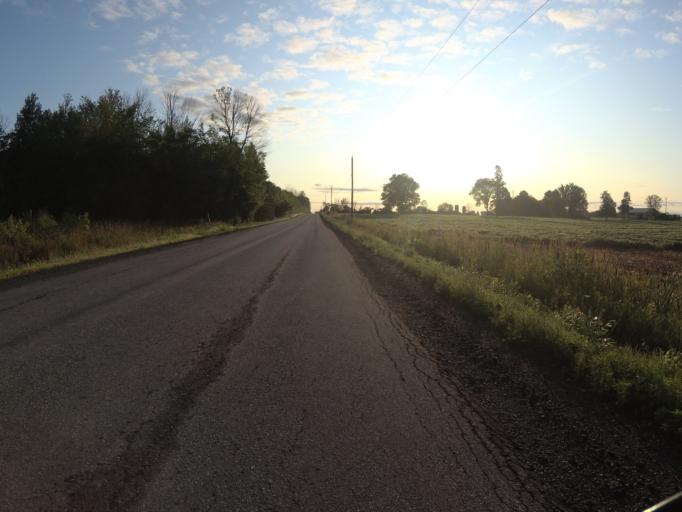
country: CA
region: Ontario
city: Casselman
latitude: 45.1540
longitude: -75.4201
